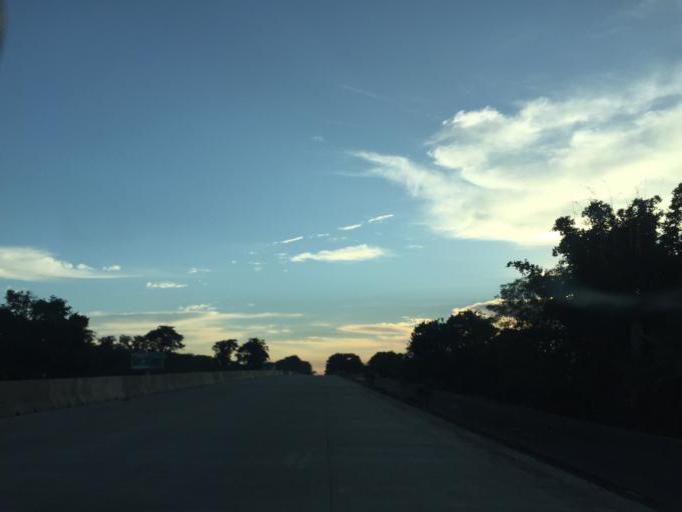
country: MX
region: Veracruz
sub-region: Ixtaczoquitlan
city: Buenavista
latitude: 18.9075
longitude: -97.0230
